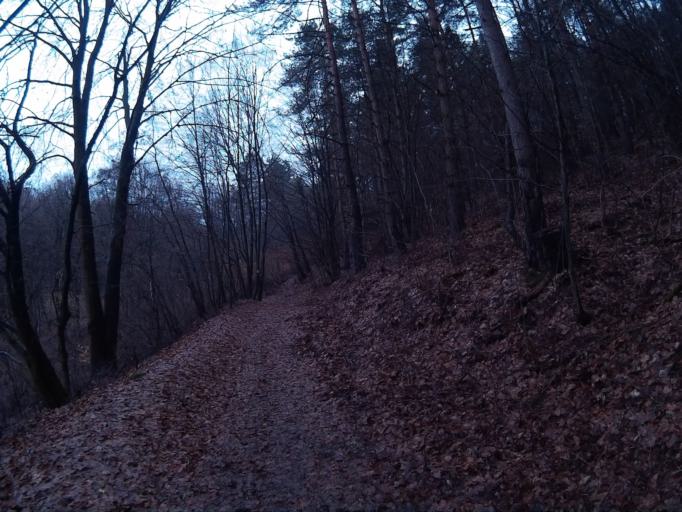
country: HU
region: Borsod-Abauj-Zemplen
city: Sarospatak
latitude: 48.4697
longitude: 21.4719
